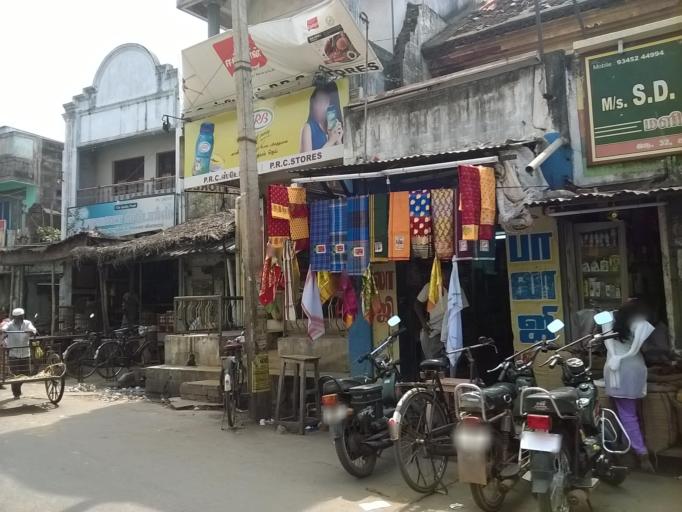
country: IN
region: Tamil Nadu
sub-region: Cuddalore
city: Panruti
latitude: 11.7740
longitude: 79.5502
